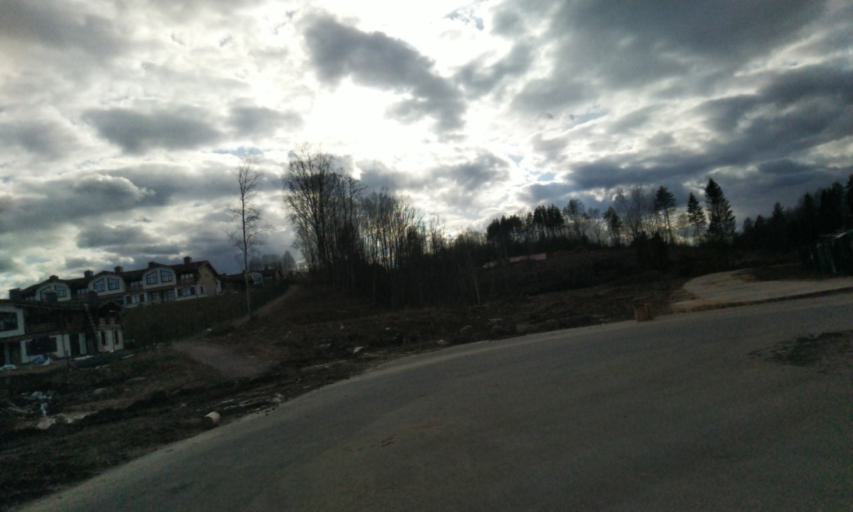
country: RU
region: Leningrad
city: Bugry
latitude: 60.1263
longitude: 30.4361
